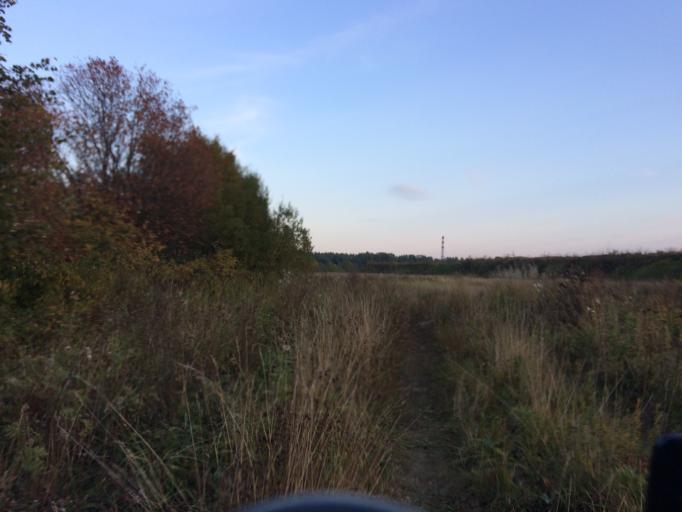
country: RU
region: Mariy-El
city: Yoshkar-Ola
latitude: 56.6498
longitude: 47.9227
